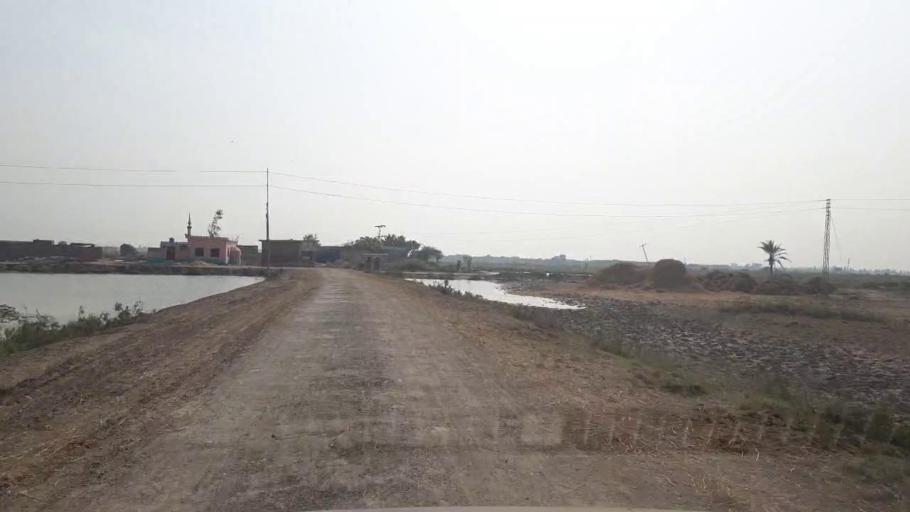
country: PK
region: Sindh
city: Tando Muhammad Khan
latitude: 25.0492
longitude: 68.3935
